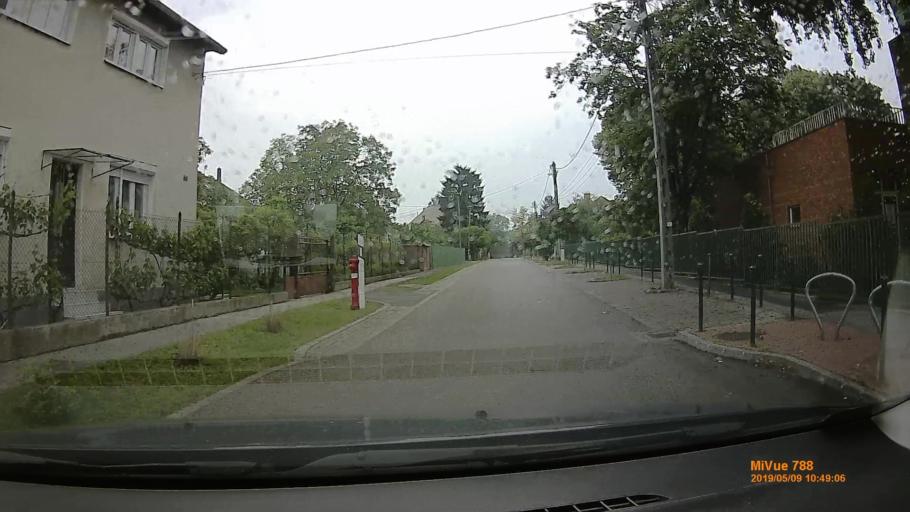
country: HU
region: Budapest
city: Budapest XVI. keruelet
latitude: 47.5198
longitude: 19.1569
